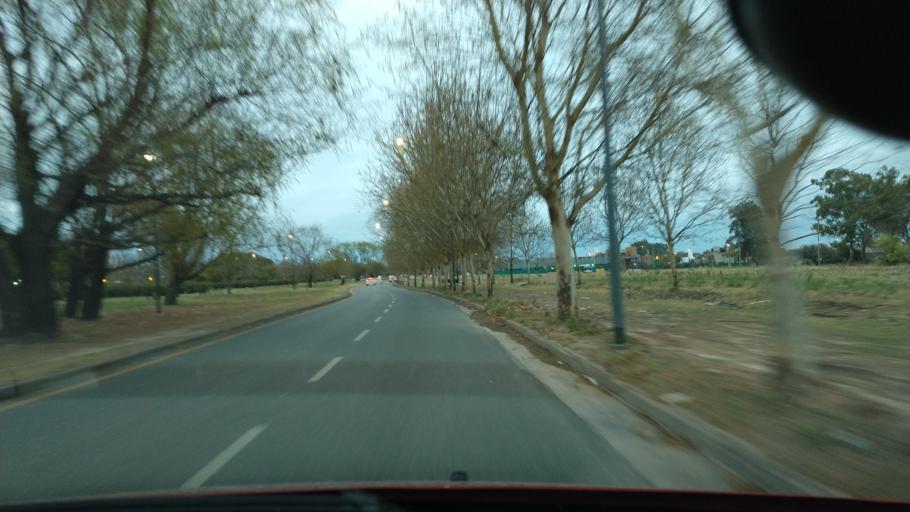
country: AR
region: Cordoba
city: La Calera
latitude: -31.3760
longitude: -64.2768
